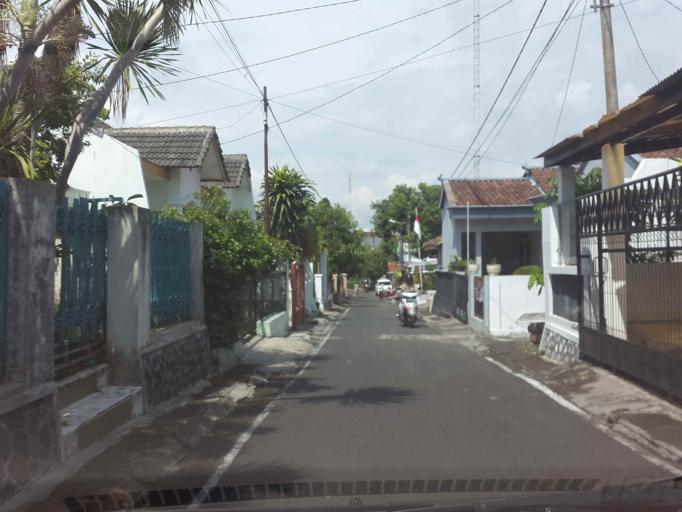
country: ID
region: Central Java
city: Salatiga
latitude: -7.3228
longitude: 110.5056
